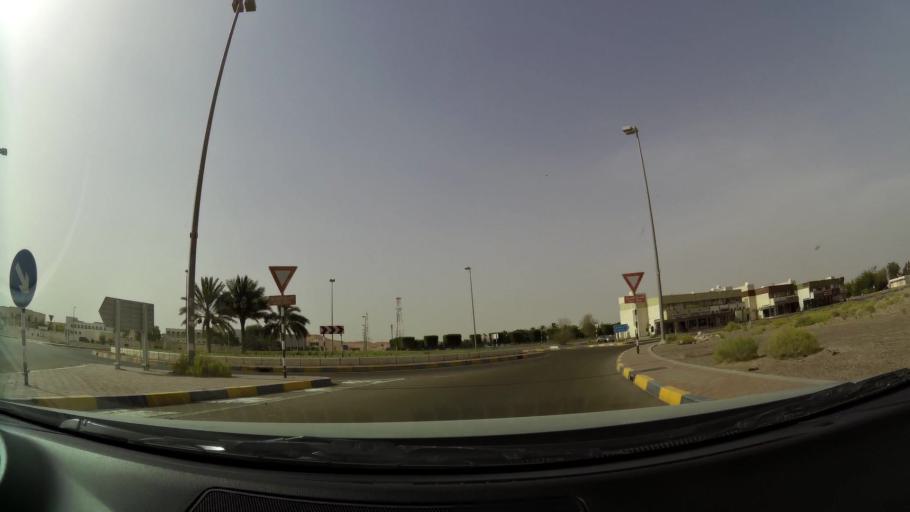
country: AE
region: Abu Dhabi
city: Al Ain
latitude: 24.2030
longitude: 55.5782
